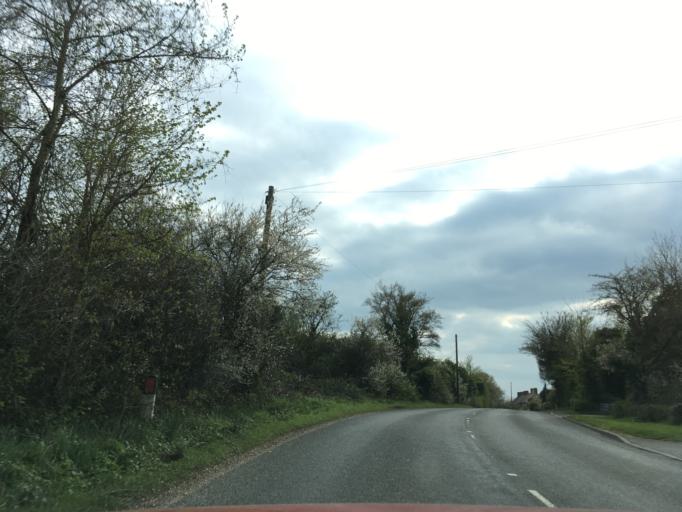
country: GB
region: England
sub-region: Oxfordshire
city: Woodstock
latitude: 51.8577
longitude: -1.3121
